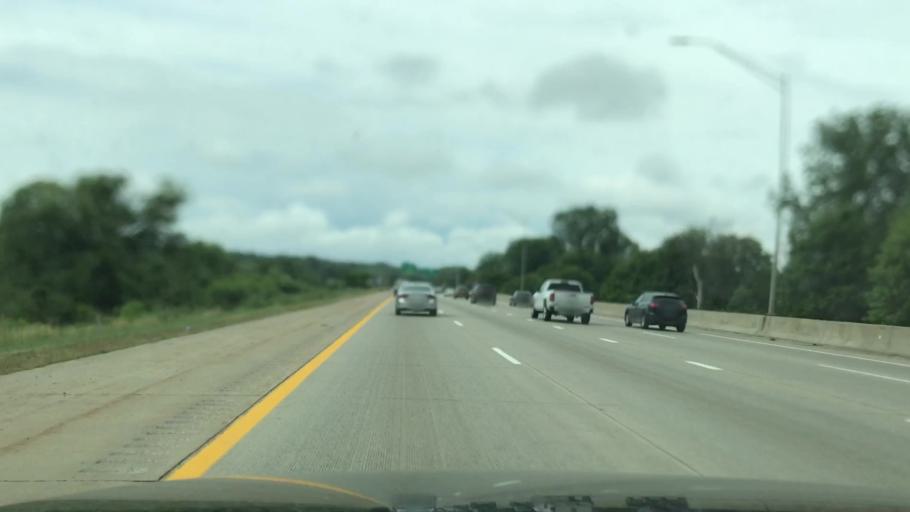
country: US
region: Michigan
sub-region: Kent County
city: Comstock Park
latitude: 43.0073
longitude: -85.6750
